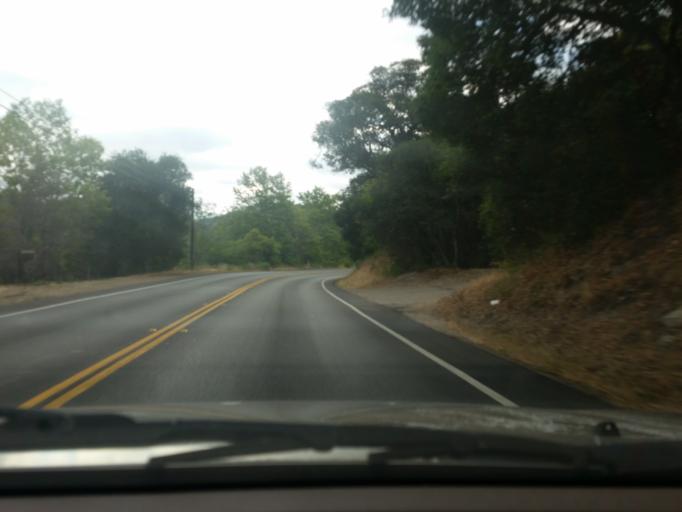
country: US
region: California
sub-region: San Luis Obispo County
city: Avila Beach
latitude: 35.1849
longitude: -120.7099
